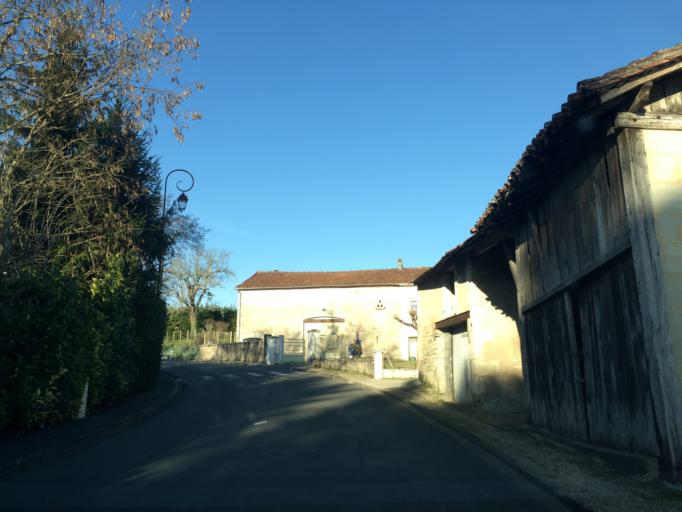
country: FR
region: Aquitaine
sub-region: Departement de la Dordogne
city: Neuvic
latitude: 45.1388
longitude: 0.4512
